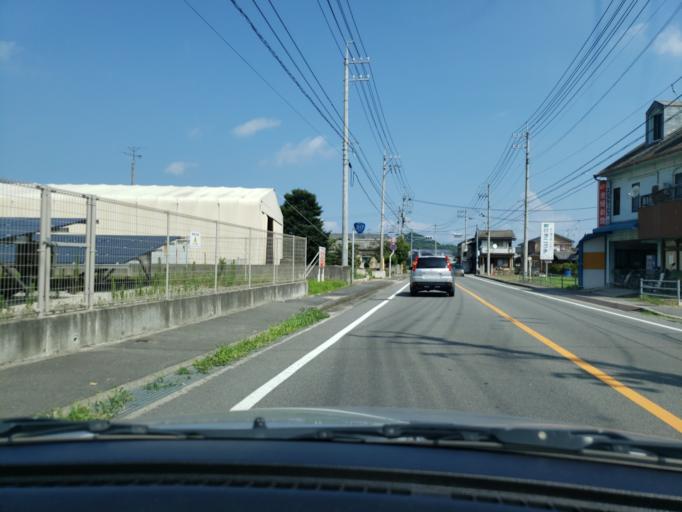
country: JP
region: Ehime
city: Hojo
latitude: 34.0968
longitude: 132.9730
